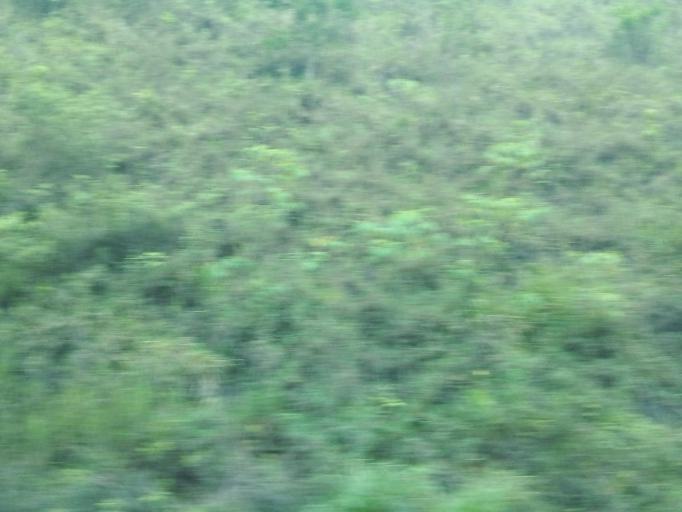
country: BR
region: Minas Gerais
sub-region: Joao Monlevade
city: Joao Monlevade
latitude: -19.8692
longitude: -43.1213
